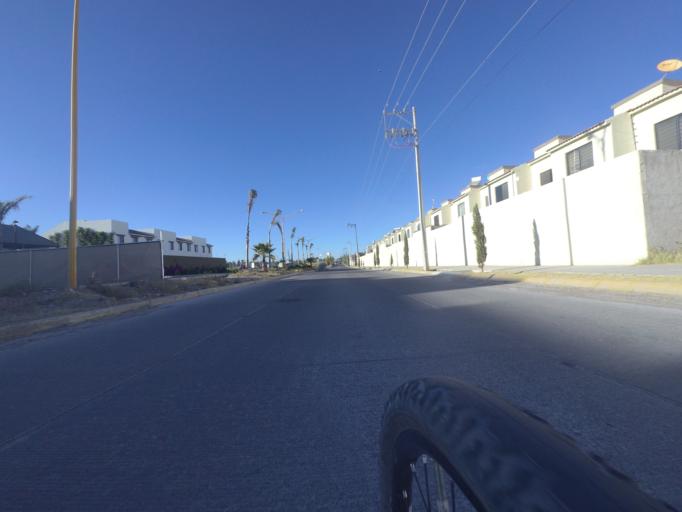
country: MX
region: Aguascalientes
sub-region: Aguascalientes
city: La Loma de los Negritos
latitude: 21.8530
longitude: -102.3459
